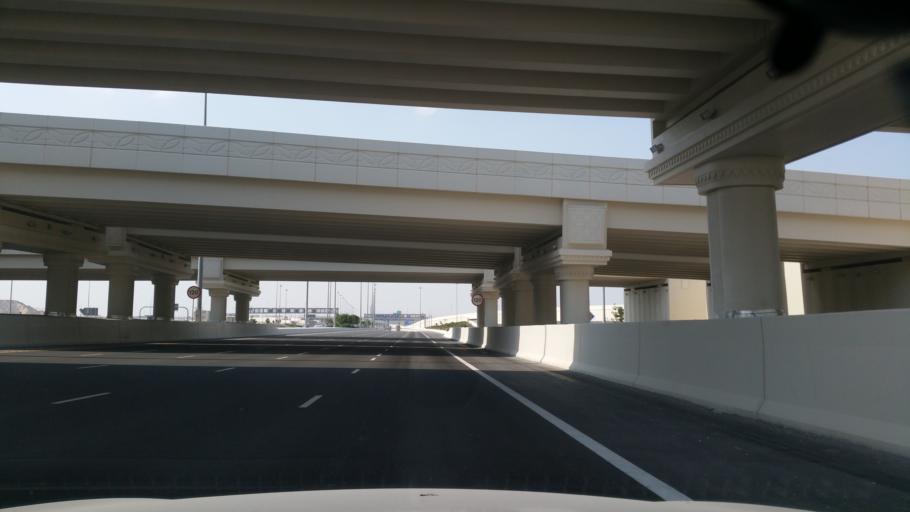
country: QA
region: Baladiyat Umm Salal
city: Umm Salal Muhammad
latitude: 25.3927
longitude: 51.4978
